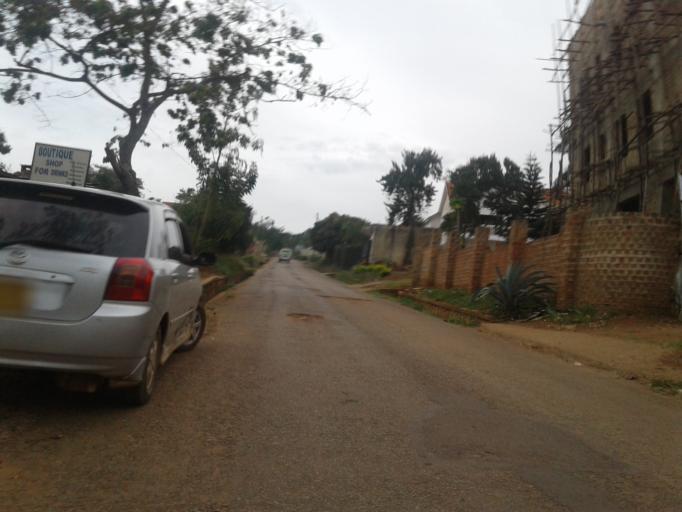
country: UG
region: Central Region
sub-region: Kampala District
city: Kampala
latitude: 0.2480
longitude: 32.6259
